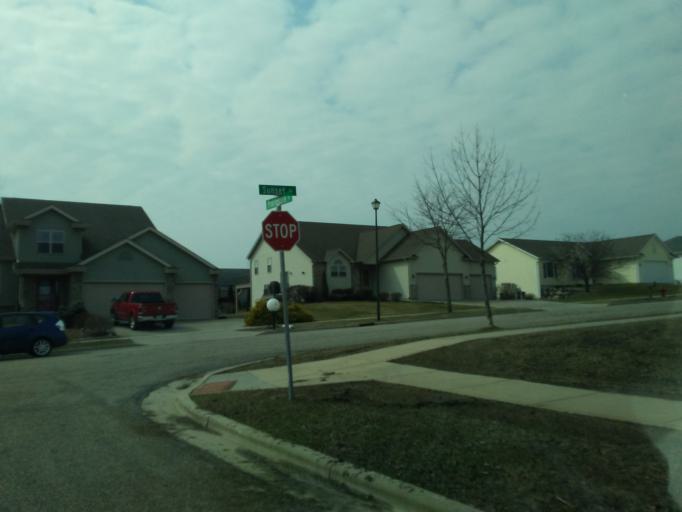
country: US
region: Wisconsin
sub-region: Columbia County
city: Lodi
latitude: 43.3098
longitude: -89.5424
